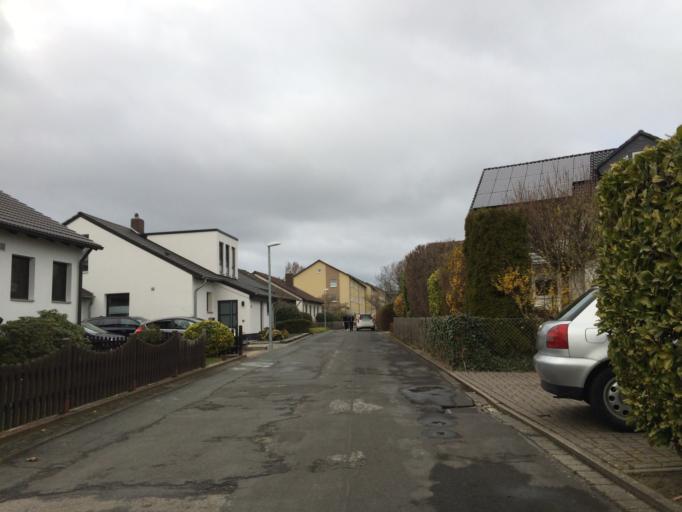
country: DE
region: Lower Saxony
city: Gehrden
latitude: 52.3045
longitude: 9.6076
